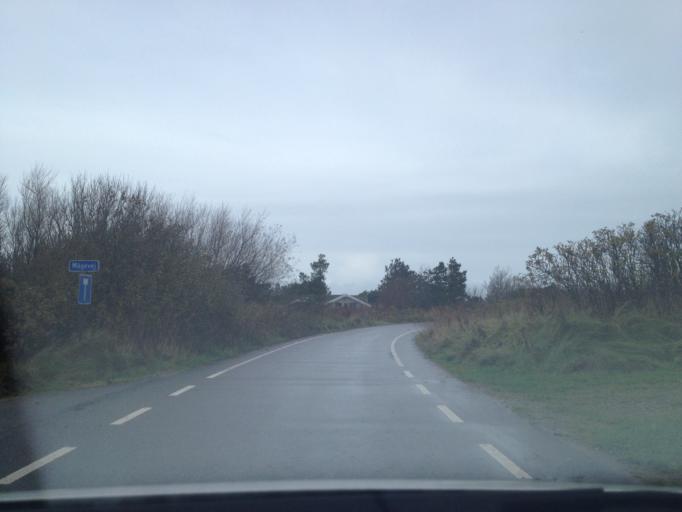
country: DE
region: Schleswig-Holstein
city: List
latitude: 55.1523
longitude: 8.5110
